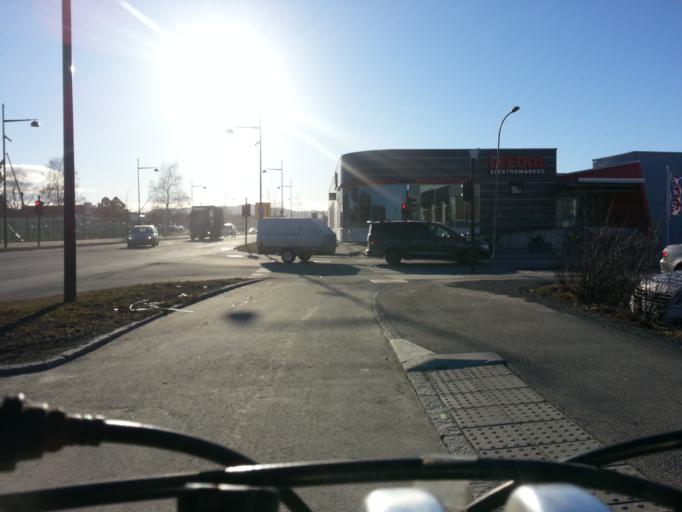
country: NO
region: Sor-Trondelag
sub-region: Trondheim
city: Trondheim
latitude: 63.4437
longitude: 10.4498
